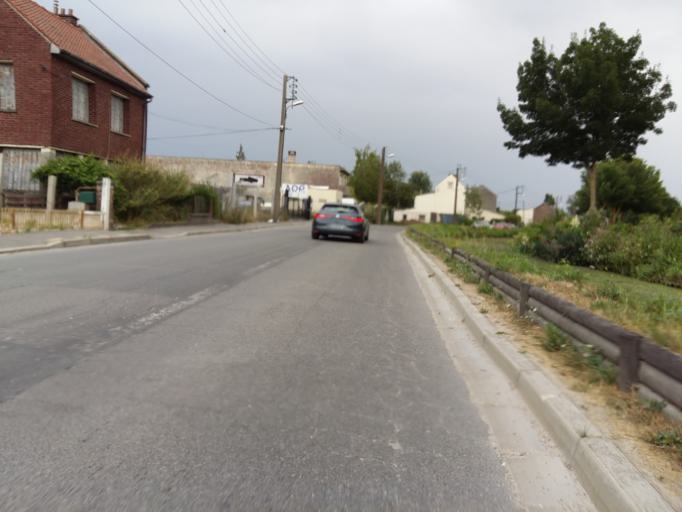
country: FR
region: Picardie
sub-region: Departement de la Somme
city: Rivery
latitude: 49.8921
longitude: 2.3210
